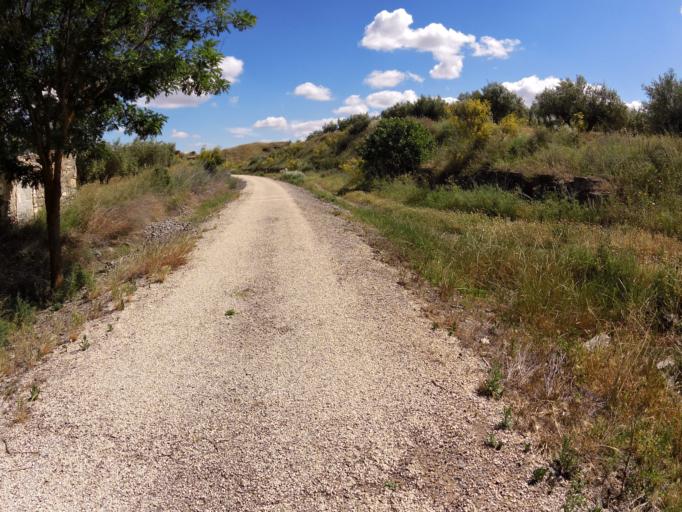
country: ES
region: Andalusia
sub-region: Provincia de Jaen
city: Alcaudete
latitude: 37.6319
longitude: -4.0836
